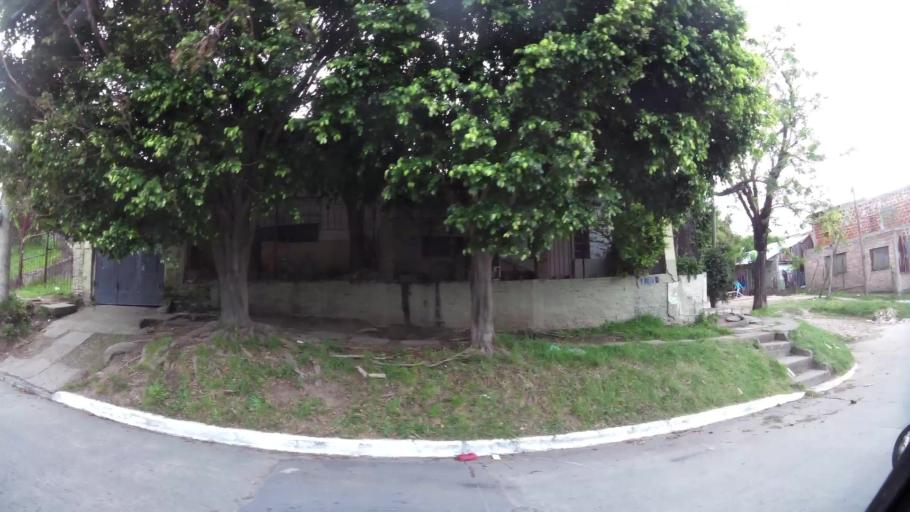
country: AR
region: Buenos Aires
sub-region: Partido de Quilmes
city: Quilmes
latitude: -34.7261
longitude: -58.2362
